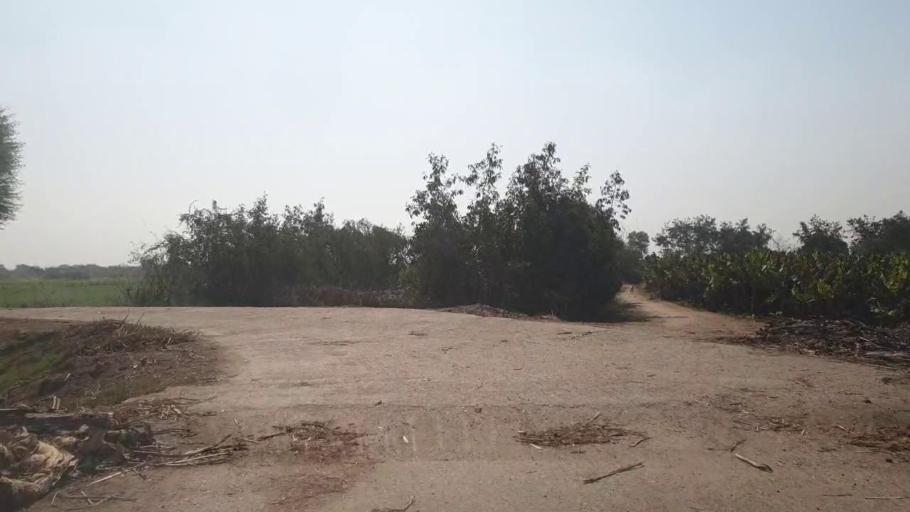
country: PK
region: Sindh
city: Tando Jam
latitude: 25.3411
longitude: 68.6020
